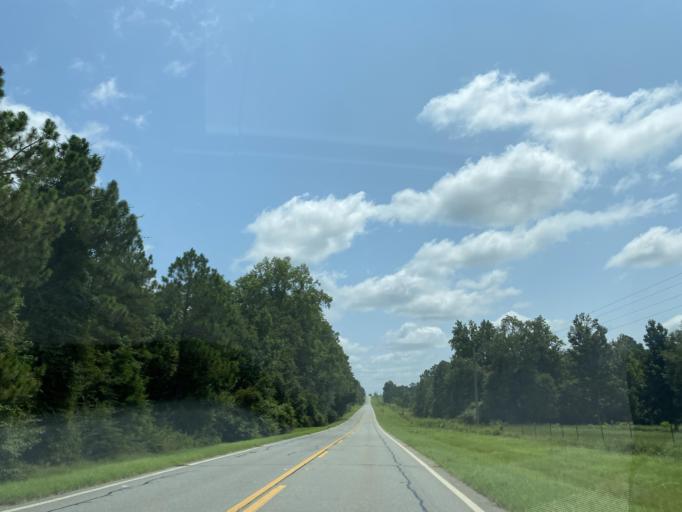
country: US
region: Georgia
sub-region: Wilcox County
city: Abbeville
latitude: 32.0097
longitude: -83.1114
